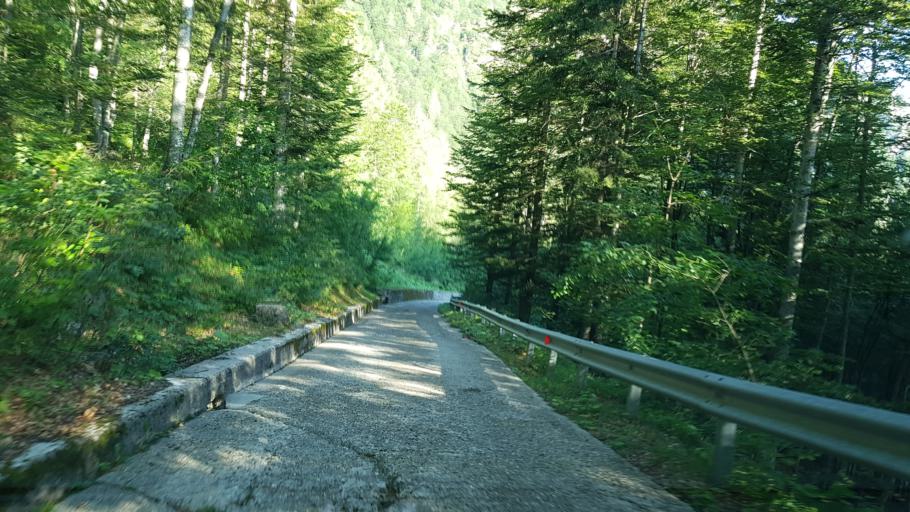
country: IT
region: Friuli Venezia Giulia
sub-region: Provincia di Udine
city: Pontebba
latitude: 46.4786
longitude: 13.2533
